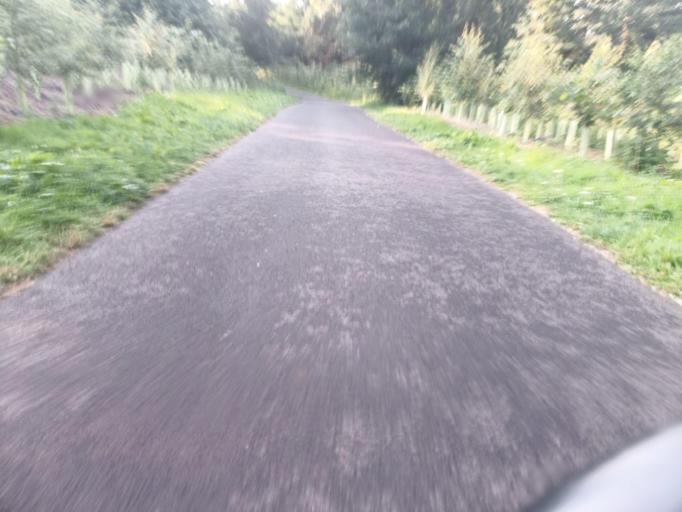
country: GB
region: Northern Ireland
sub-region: Castlereagh District
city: Dundonald
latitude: 54.5859
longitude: -5.7979
